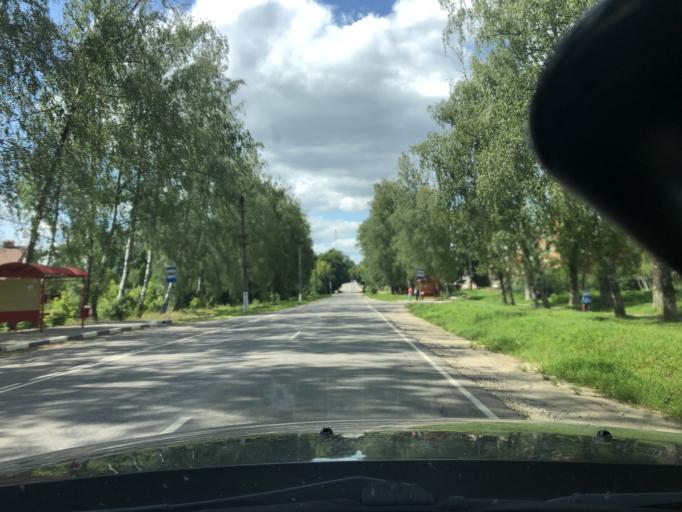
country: RU
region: Tula
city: Gorelki
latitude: 54.3376
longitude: 37.5563
